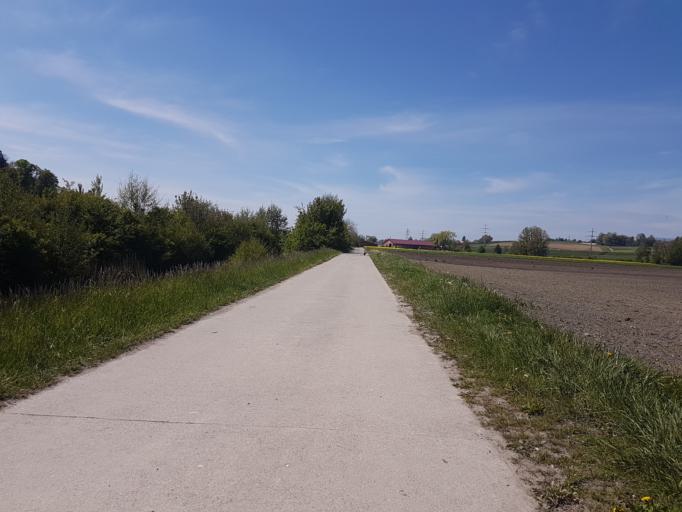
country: CH
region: Neuchatel
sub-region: Neuchatel District
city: Cornaux
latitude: 47.0314
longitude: 7.0389
